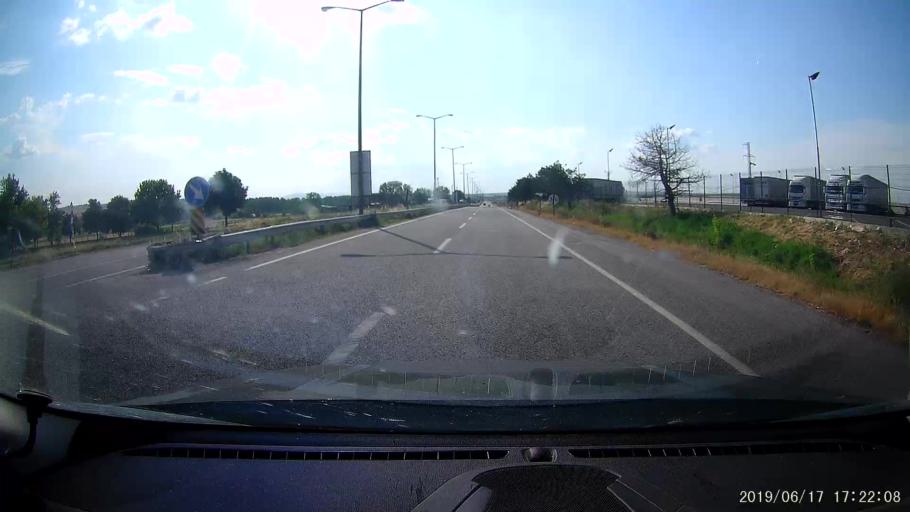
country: GR
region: East Macedonia and Thrace
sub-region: Nomos Evrou
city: Rizia
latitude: 41.7098
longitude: 26.3807
